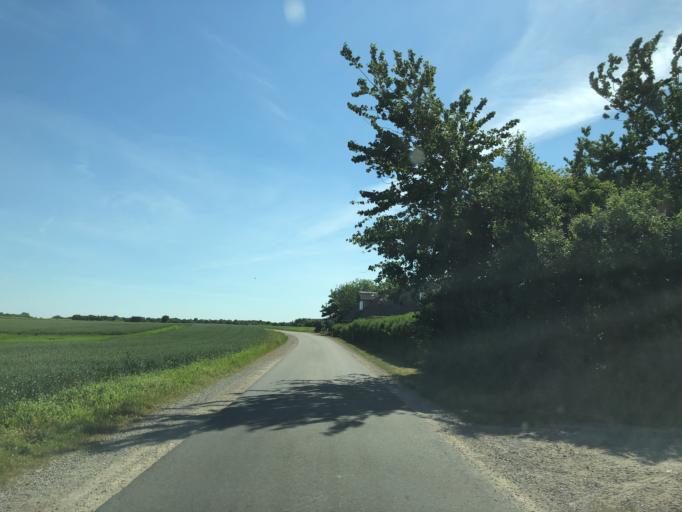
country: DK
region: Central Jutland
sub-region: Struer Kommune
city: Struer
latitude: 56.4311
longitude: 8.4738
